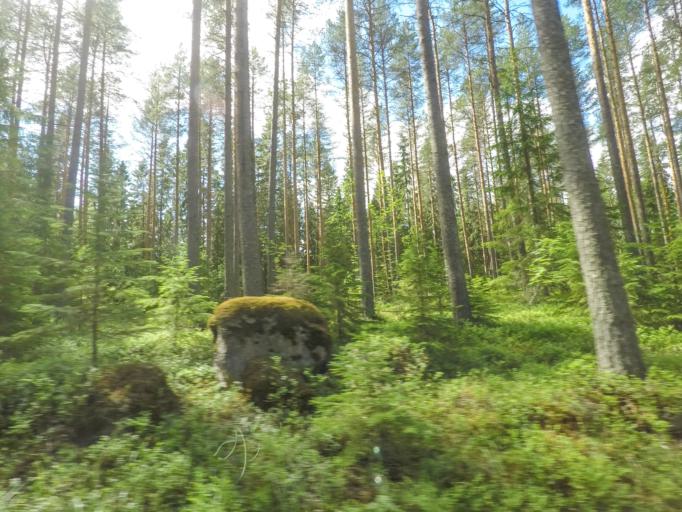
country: FI
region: Central Finland
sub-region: Jyvaeskylae
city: Hankasalmi
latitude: 62.4128
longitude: 26.6435
